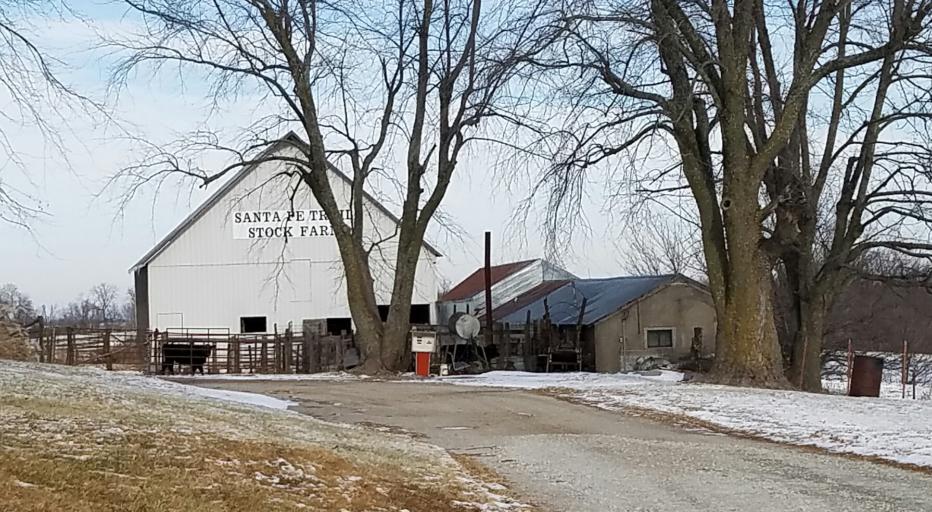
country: US
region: Missouri
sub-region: Lafayette County
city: Higginsville
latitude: 39.1953
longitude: -93.6378
